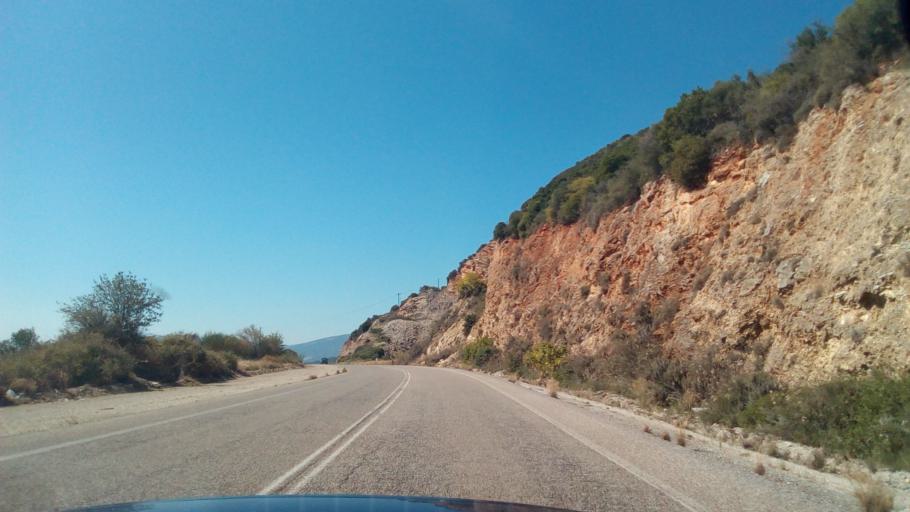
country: GR
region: West Greece
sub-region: Nomos Achaias
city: Kamarai
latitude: 38.4059
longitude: 21.9610
